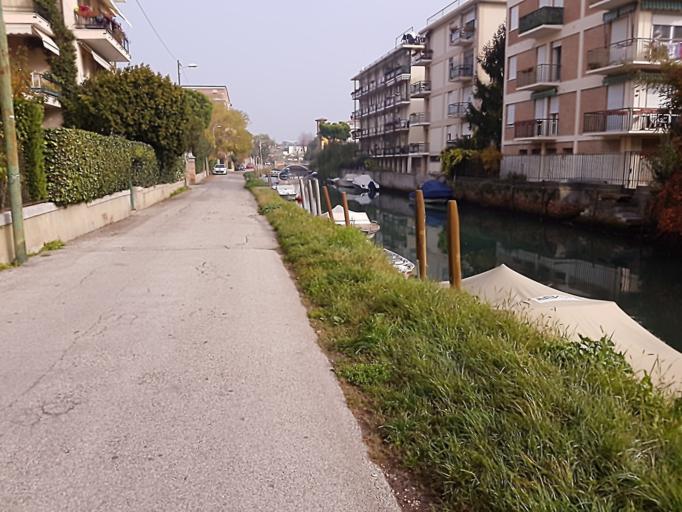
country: IT
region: Veneto
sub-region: Provincia di Venezia
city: Lido
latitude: 45.4082
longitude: 12.3673
